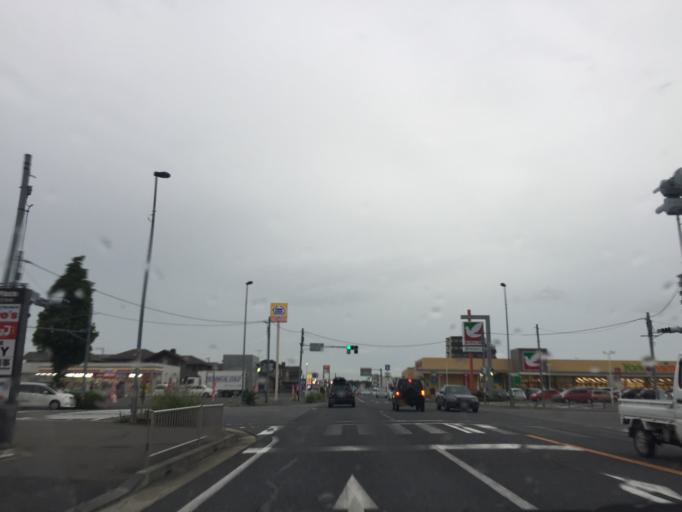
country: JP
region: Ibaraki
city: Naka
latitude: 36.0084
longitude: 140.1555
